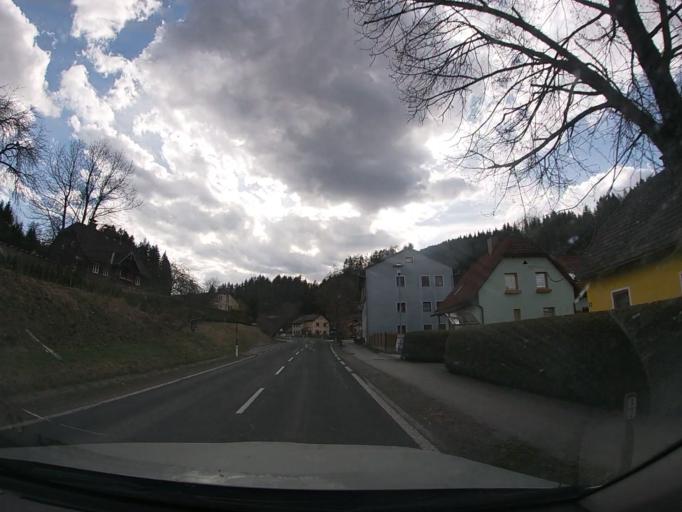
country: AT
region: Styria
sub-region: Politischer Bezirk Murau
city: Sankt Blasen
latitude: 47.0999
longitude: 14.3277
